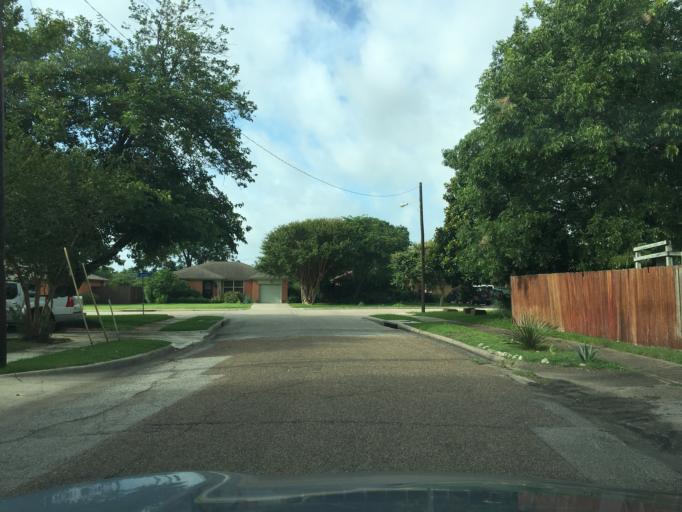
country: US
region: Texas
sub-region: Dallas County
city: Richardson
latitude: 32.9457
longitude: -96.7258
